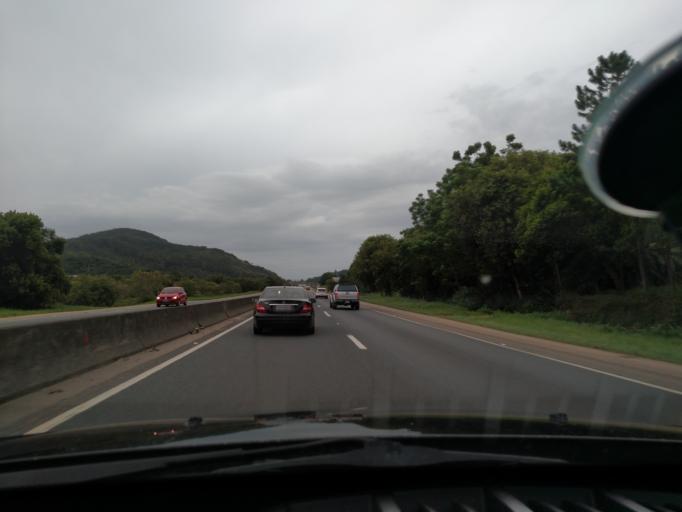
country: BR
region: Santa Catarina
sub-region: Tijucas
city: Tijucas
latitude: -27.3095
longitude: -48.6330
